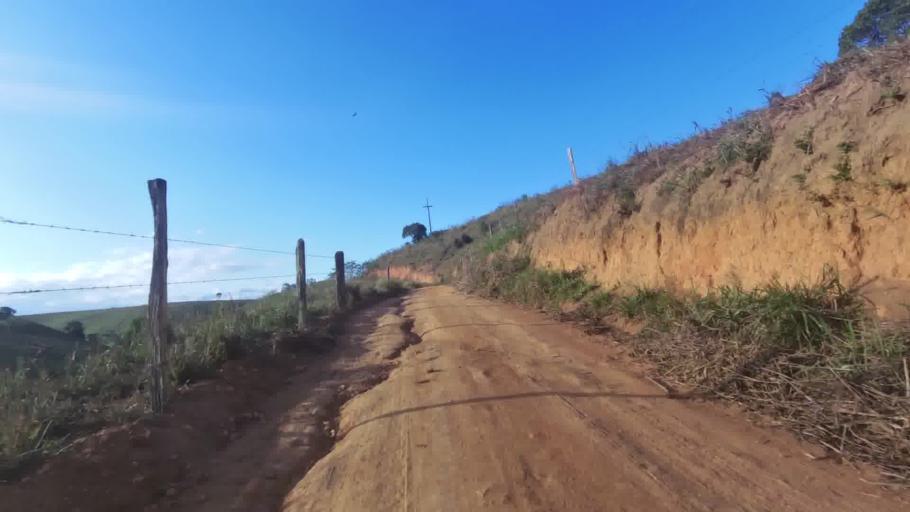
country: BR
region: Espirito Santo
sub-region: Marataizes
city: Marataizes
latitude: -21.1611
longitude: -41.0367
